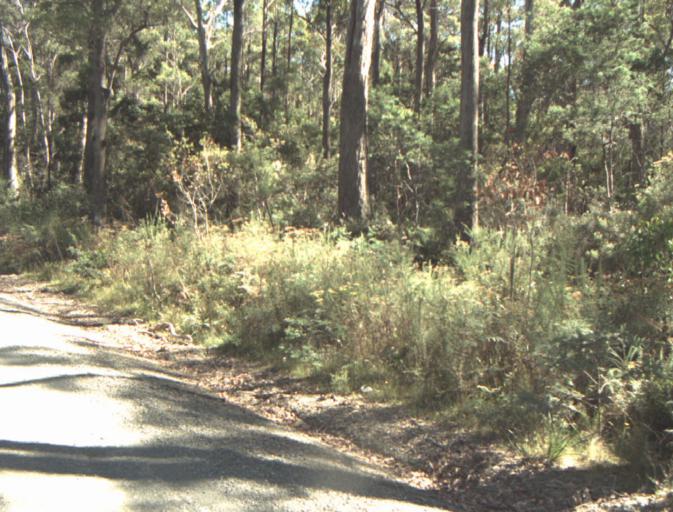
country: AU
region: Tasmania
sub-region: Launceston
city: Newstead
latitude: -41.3763
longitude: 147.2864
